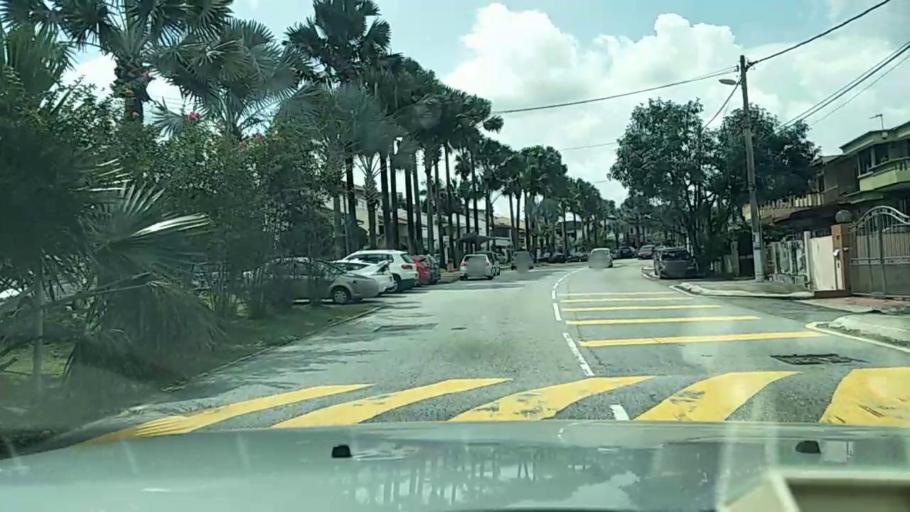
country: MY
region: Kuala Lumpur
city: Kuala Lumpur
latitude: 3.1303
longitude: 101.6736
